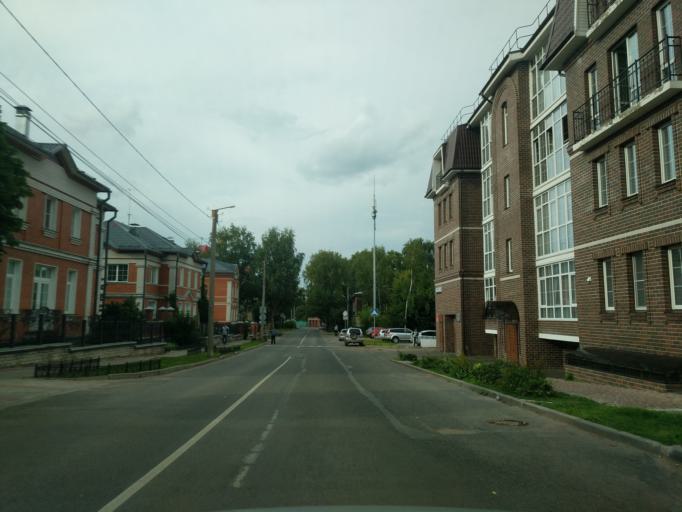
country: RU
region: Kirov
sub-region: Kirovo-Chepetskiy Rayon
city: Kirov
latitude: 58.5980
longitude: 49.6881
